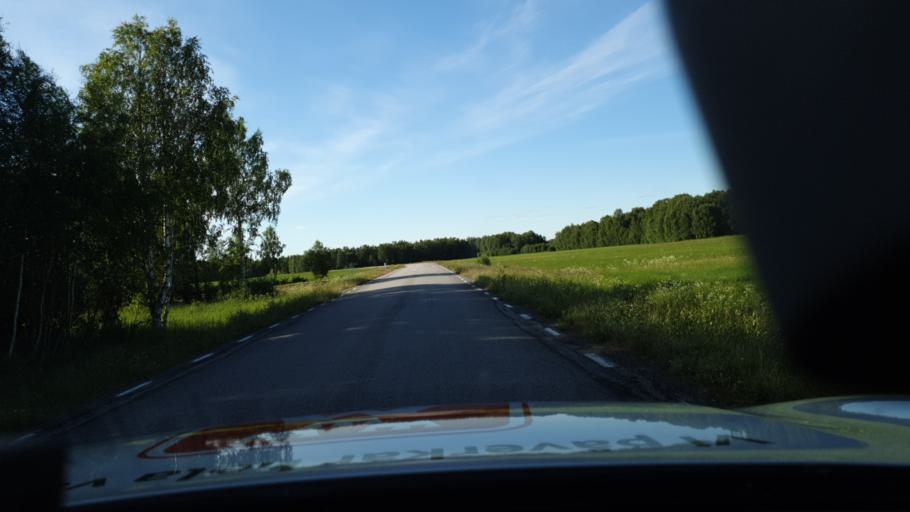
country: SE
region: Norrbotten
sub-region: Kalix Kommun
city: Toere
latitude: 65.8795
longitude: 22.6667
